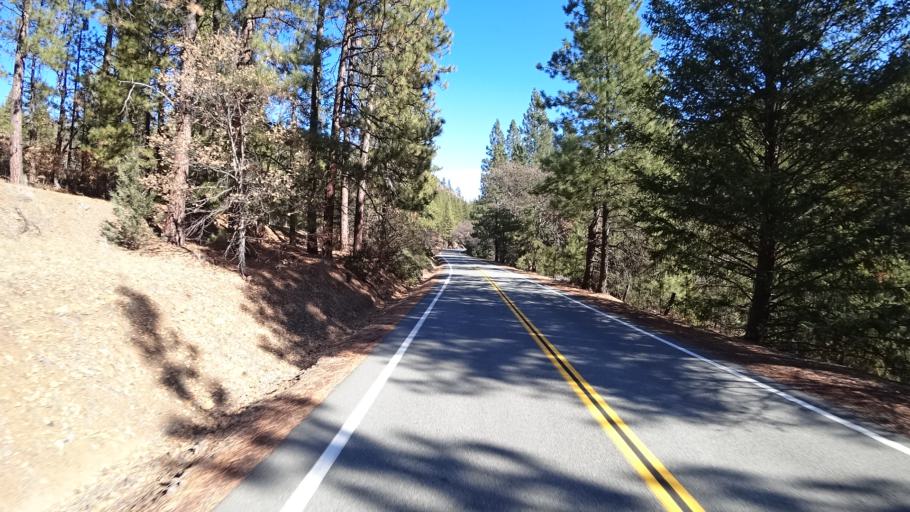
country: US
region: California
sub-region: Siskiyou County
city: Weed
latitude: 41.4568
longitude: -122.6342
